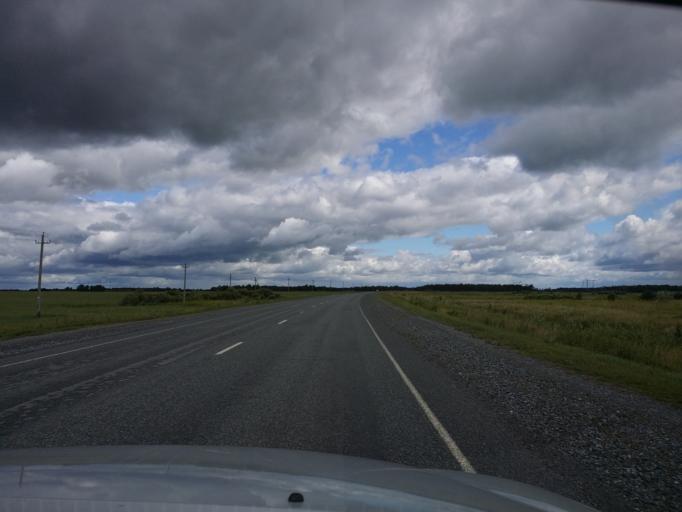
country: RU
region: Tjumen
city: Sumkino
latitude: 57.8632
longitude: 68.0515
